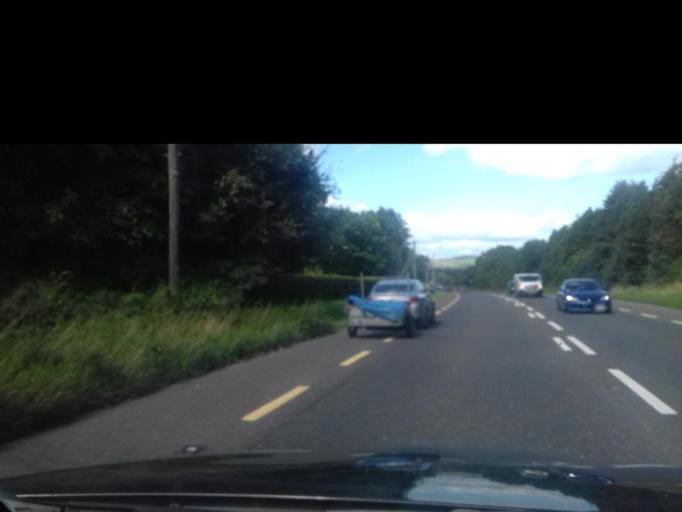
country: IE
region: Munster
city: Carrick-on-Suir
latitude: 52.4253
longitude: -7.4718
